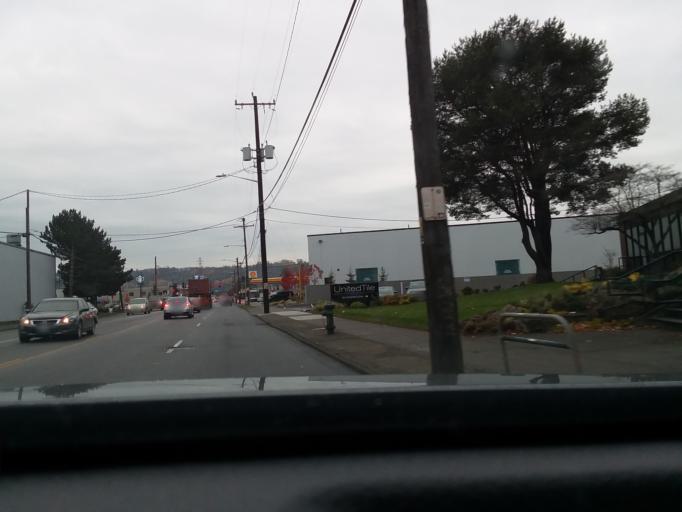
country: US
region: Washington
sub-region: King County
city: White Center
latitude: 47.5469
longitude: -122.3239
